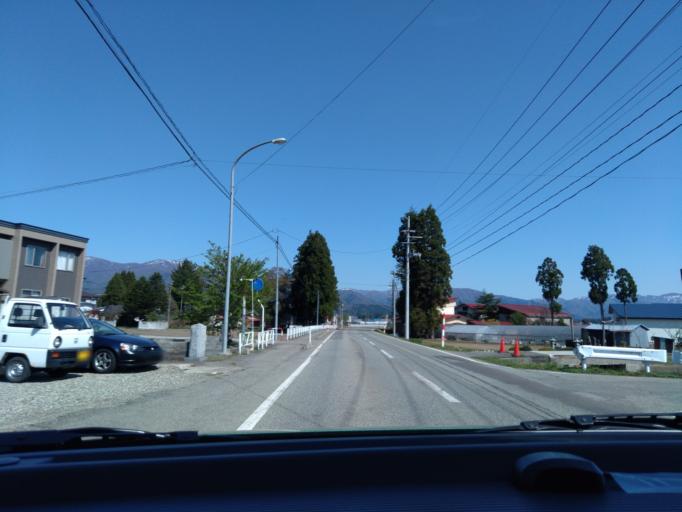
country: JP
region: Akita
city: Kakunodatemachi
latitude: 39.5747
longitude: 140.5729
